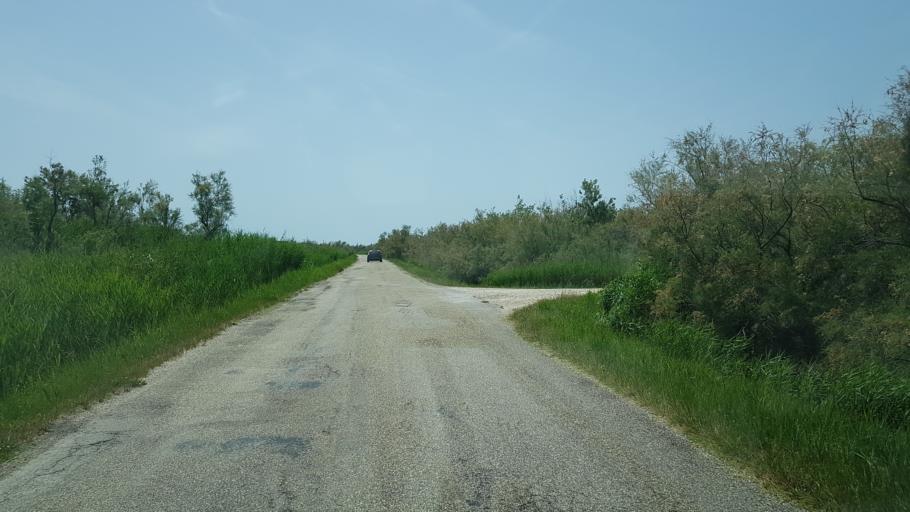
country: FR
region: Provence-Alpes-Cote d'Azur
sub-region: Departement des Bouches-du-Rhone
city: Arles
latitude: 43.4795
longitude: 4.6477
